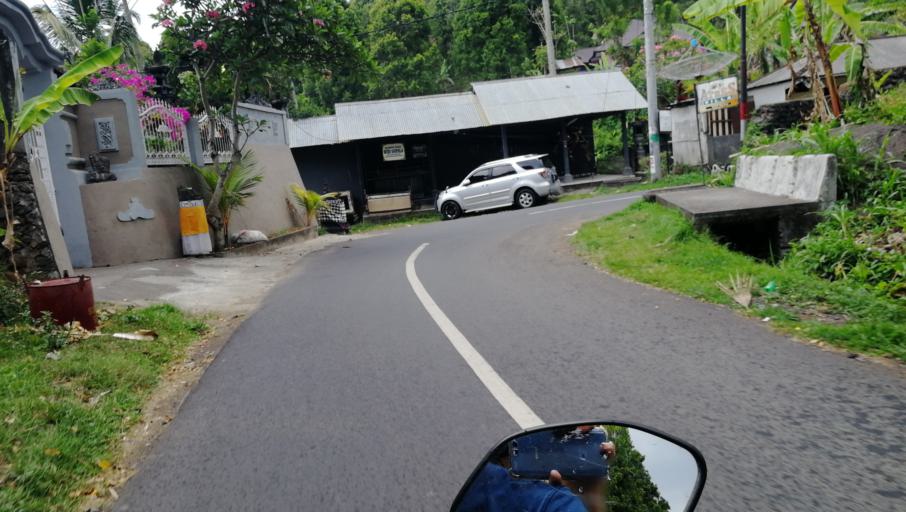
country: ID
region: Bali
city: Banjar Pedawa
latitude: -8.2638
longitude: 115.0296
